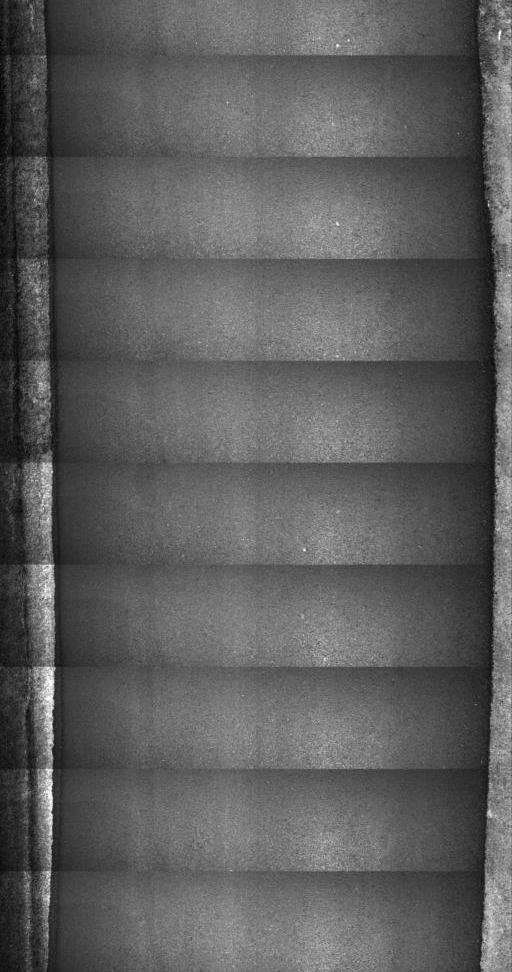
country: US
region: Vermont
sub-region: Orange County
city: Chelsea
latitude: 43.9605
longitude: -72.5517
